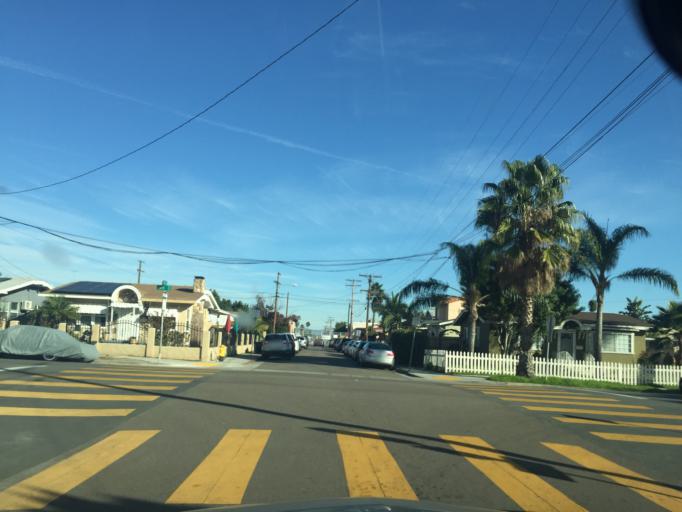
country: US
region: California
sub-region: San Diego County
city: San Diego
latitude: 32.7516
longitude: -117.1195
